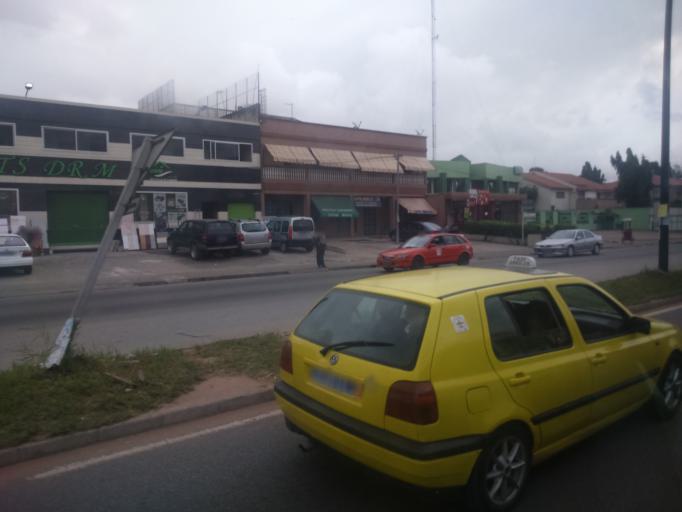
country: CI
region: Lagunes
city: Abobo
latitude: 5.3869
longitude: -3.9930
